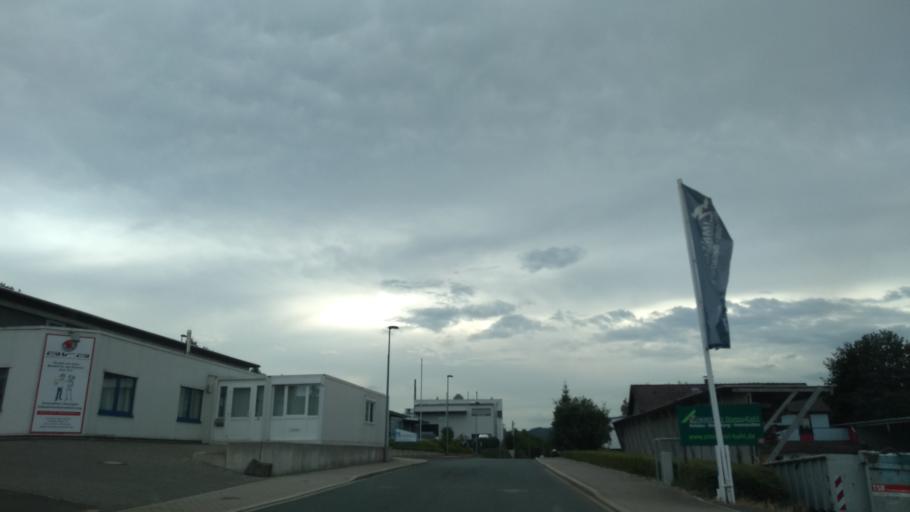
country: DE
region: North Rhine-Westphalia
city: Plettenberg
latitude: 51.1956
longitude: 7.8332
